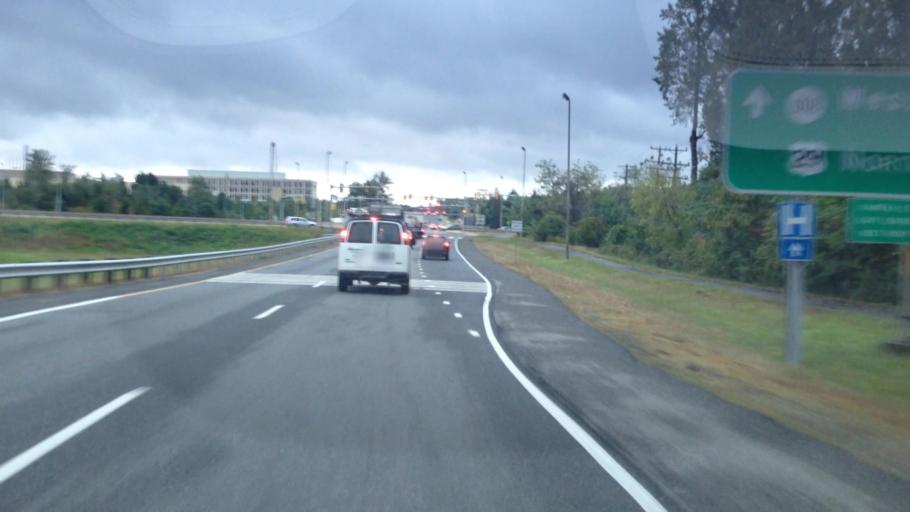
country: US
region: Virginia
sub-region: Fairfax County
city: Greenbriar
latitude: 38.8438
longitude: -77.3742
